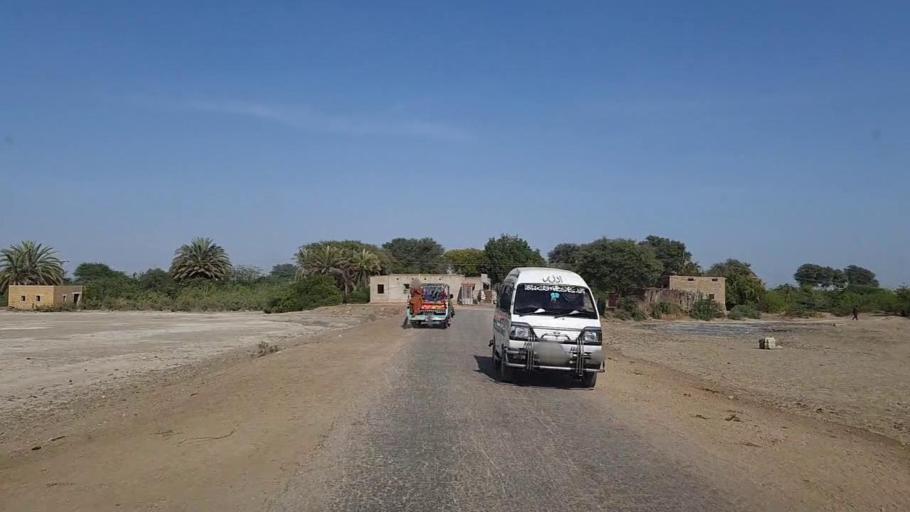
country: PK
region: Sindh
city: Kotri
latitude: 25.1634
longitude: 68.2598
